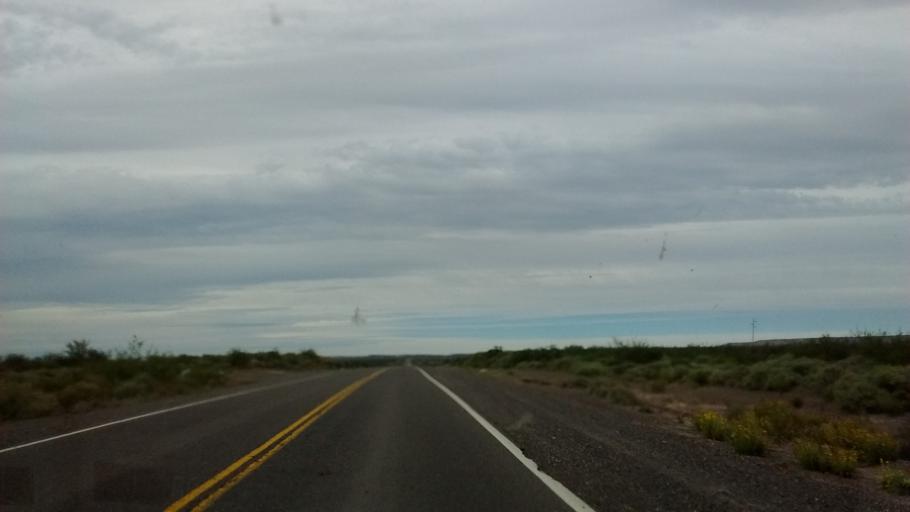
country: AR
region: Rio Negro
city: Catriel
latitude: -38.1270
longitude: -67.9329
